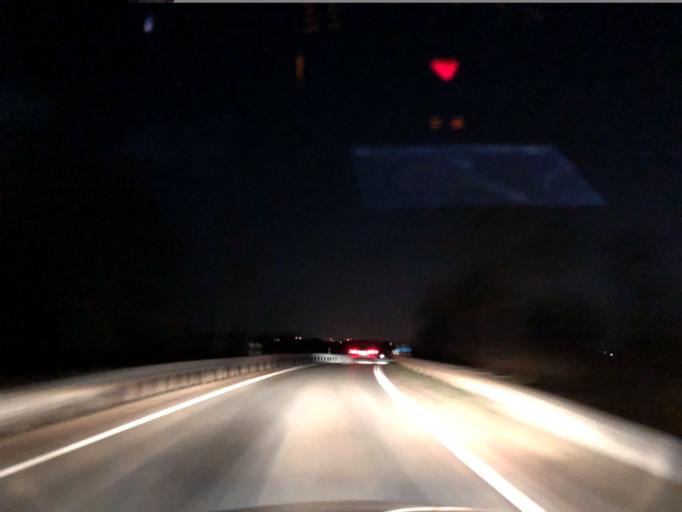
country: DE
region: Hesse
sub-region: Regierungsbezirk Darmstadt
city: Walluf
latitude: 50.0454
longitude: 8.1555
